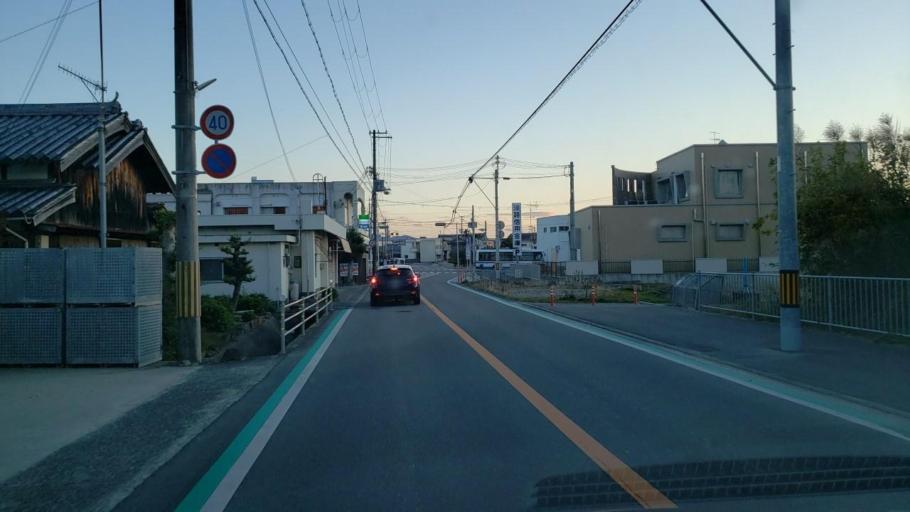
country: JP
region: Hyogo
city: Fukura
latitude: 34.3236
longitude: 134.7726
